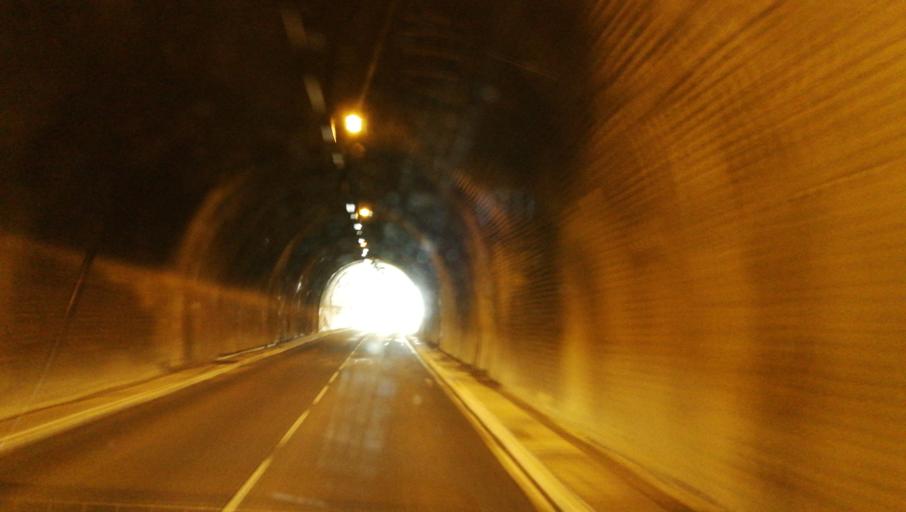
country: FR
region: Rhone-Alpes
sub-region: Departement de la Drome
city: Die
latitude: 44.8385
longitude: 5.3985
